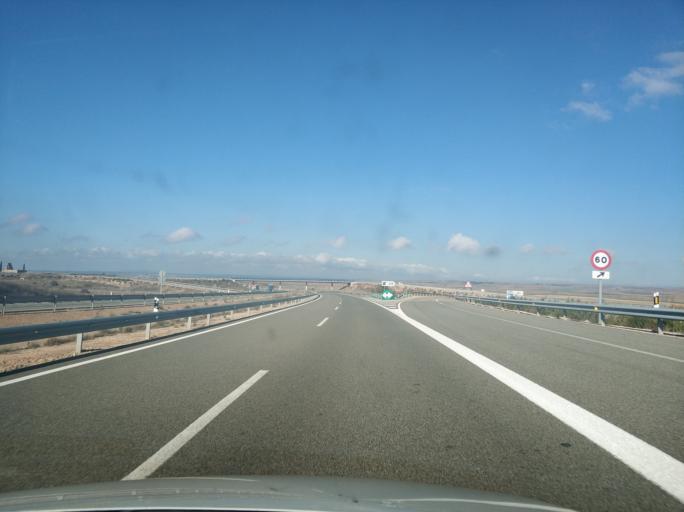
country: ES
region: Castille and Leon
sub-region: Provincia de Soria
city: Adradas
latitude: 41.3812
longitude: -2.4660
